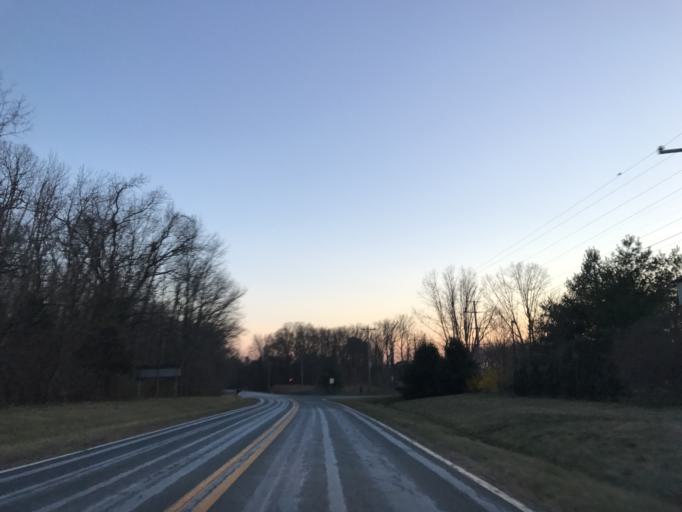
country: US
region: Maryland
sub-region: Queen Anne's County
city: Centreville
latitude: 39.0309
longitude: -76.0199
